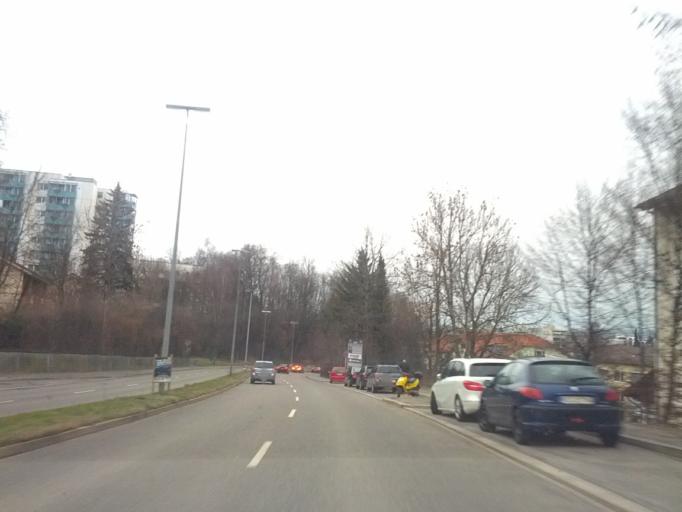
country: DE
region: Bavaria
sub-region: Swabia
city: Kempten (Allgaeu)
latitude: 47.7322
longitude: 10.3056
